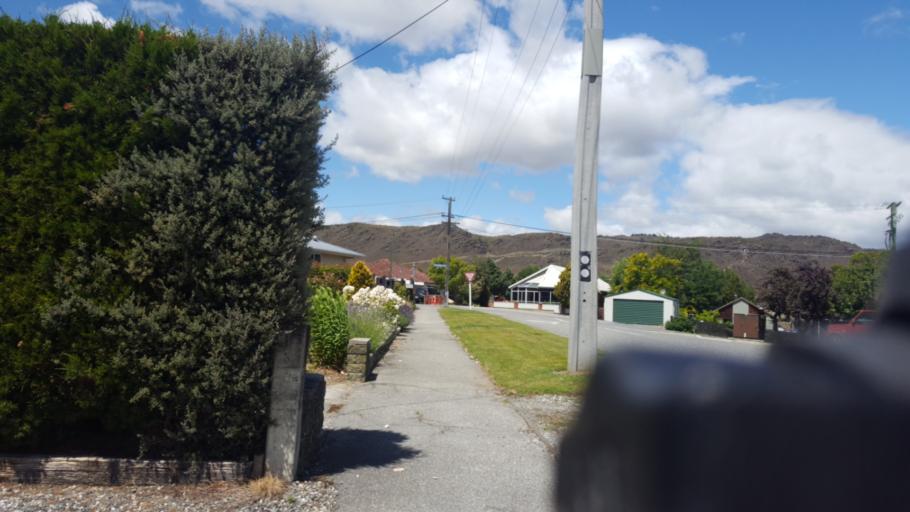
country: NZ
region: Otago
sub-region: Queenstown-Lakes District
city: Wanaka
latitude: -45.2480
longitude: 169.3940
